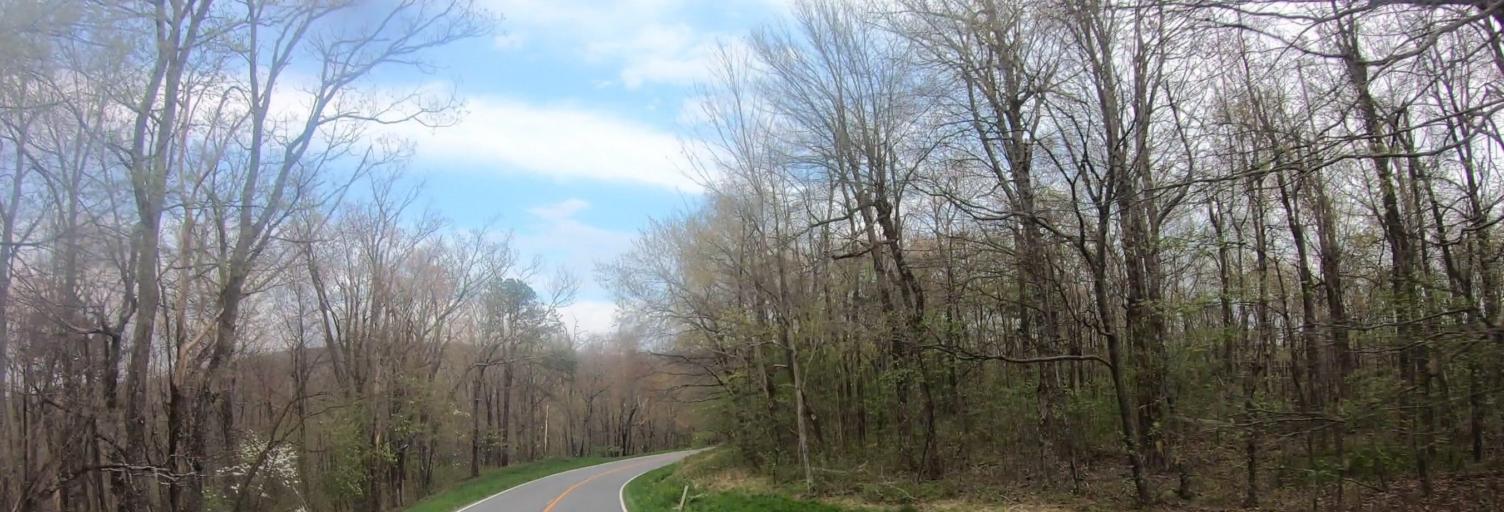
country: US
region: Virginia
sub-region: Rockingham County
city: Elkton
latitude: 38.2927
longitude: -78.6437
